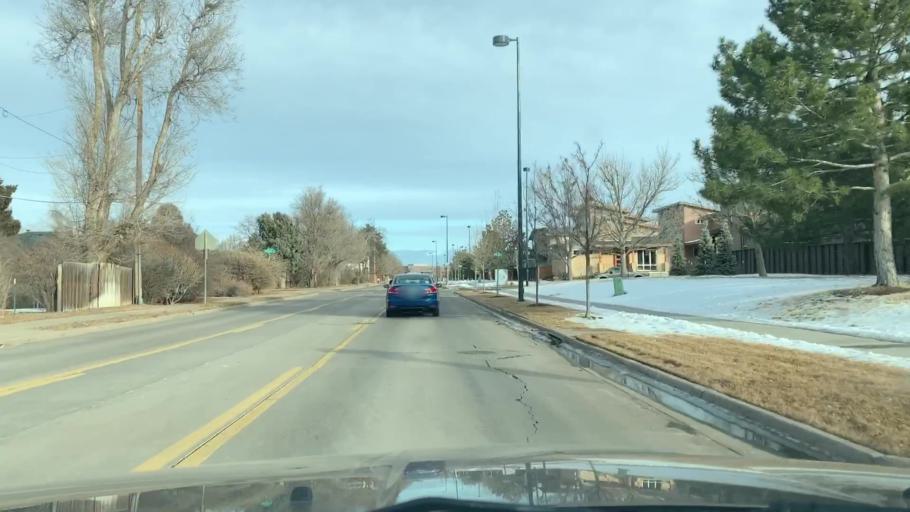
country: US
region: Colorado
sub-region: Arapahoe County
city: Glendale
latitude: 39.7183
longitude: -104.9116
